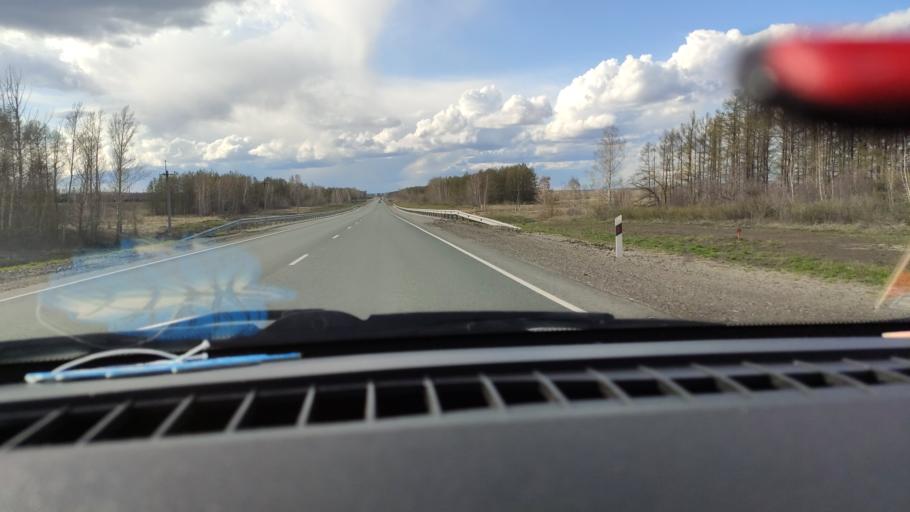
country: RU
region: Saratov
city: Shikhany
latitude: 52.1551
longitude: 47.1800
